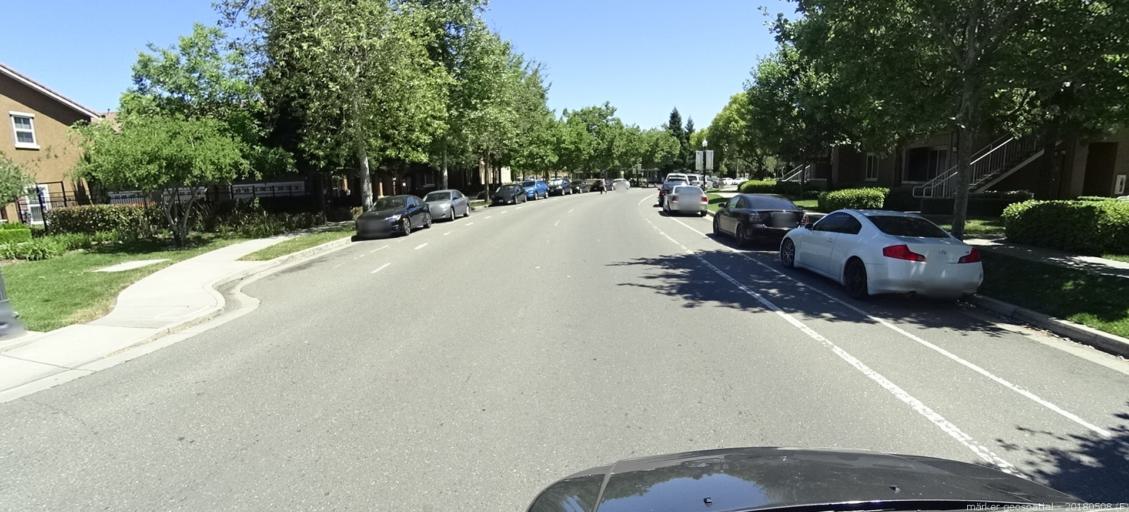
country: US
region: California
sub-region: Yolo County
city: West Sacramento
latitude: 38.6603
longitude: -121.5253
